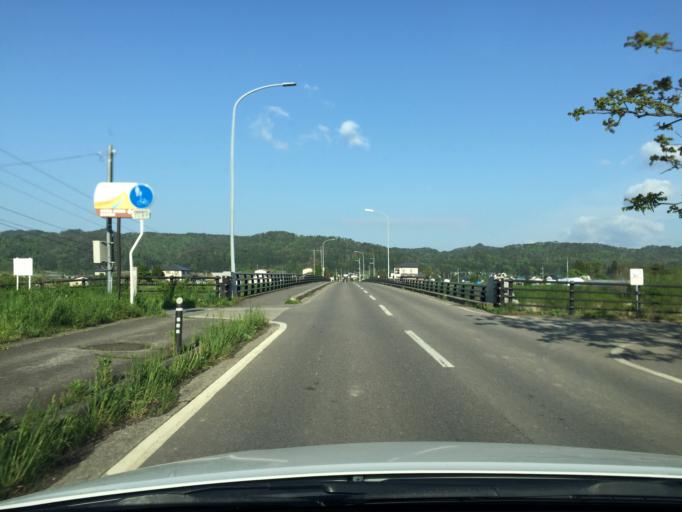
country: JP
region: Fukushima
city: Kitakata
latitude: 37.6656
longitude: 139.8593
